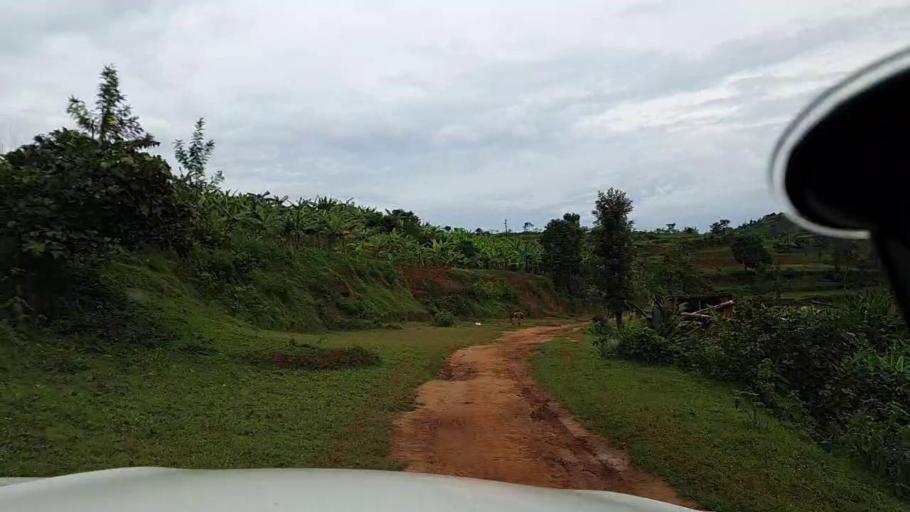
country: RW
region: Southern Province
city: Gitarama
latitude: -2.1158
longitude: 29.6446
